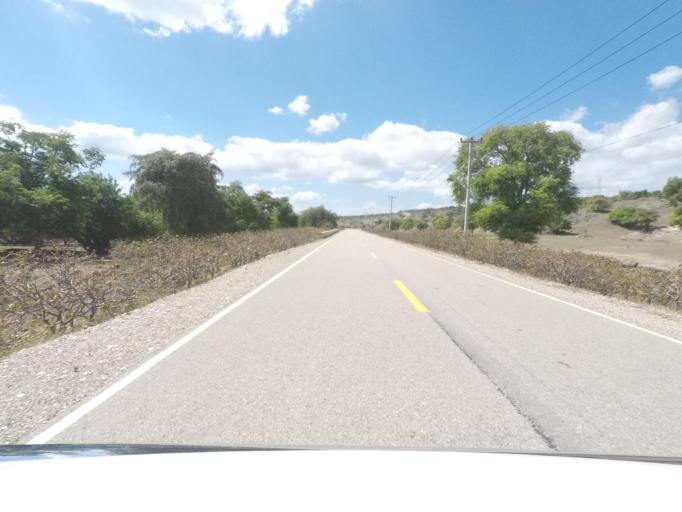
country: TL
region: Baucau
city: Baucau
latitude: -8.4377
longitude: 126.6636
